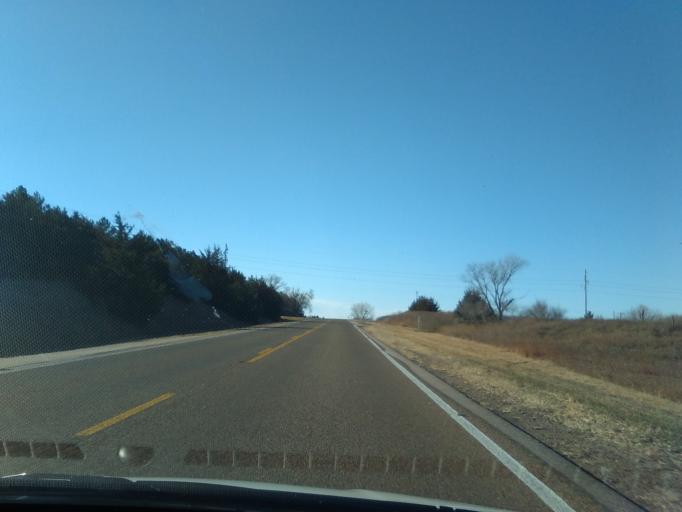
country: US
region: Nebraska
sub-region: Adams County
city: Hastings
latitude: 40.4373
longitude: -98.3704
